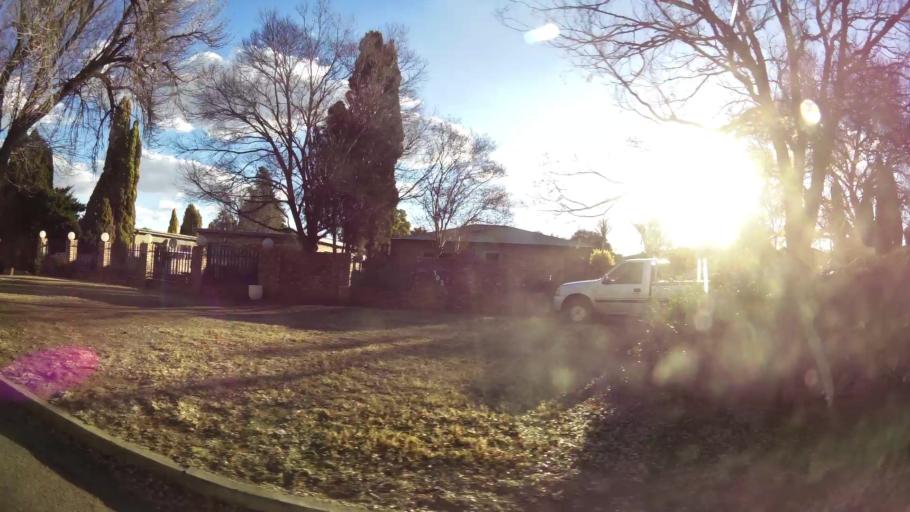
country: ZA
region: North-West
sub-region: Dr Kenneth Kaunda District Municipality
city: Potchefstroom
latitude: -26.7397
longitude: 27.0887
